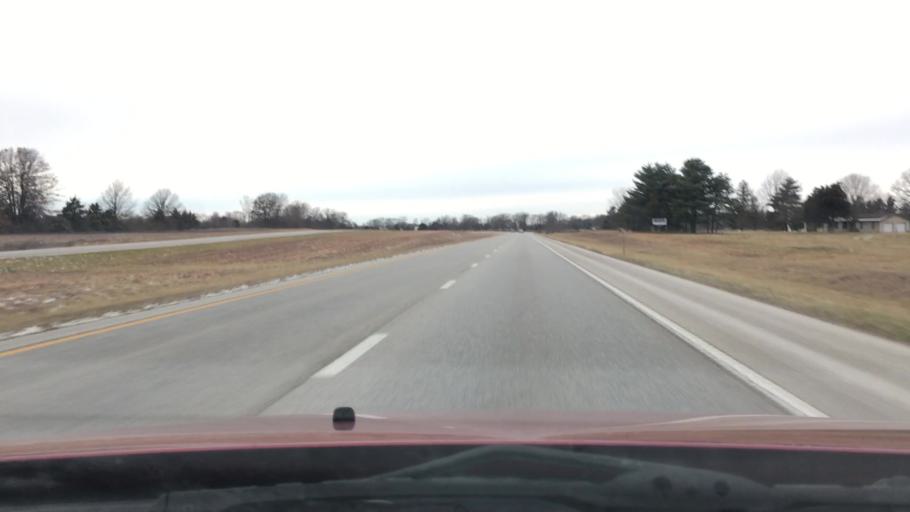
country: US
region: Missouri
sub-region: Webster County
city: Seymour
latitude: 37.1650
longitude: -92.8003
